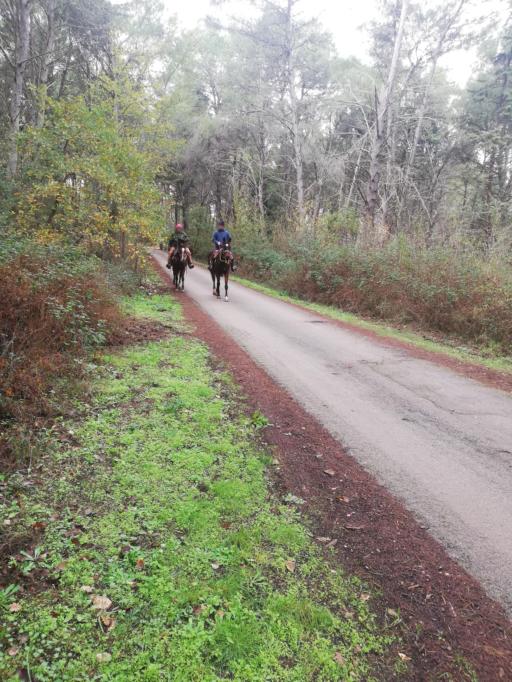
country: IT
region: Apulia
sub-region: Provincia di Bari
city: Cassano delle Murge
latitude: 40.8737
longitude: 16.6938
